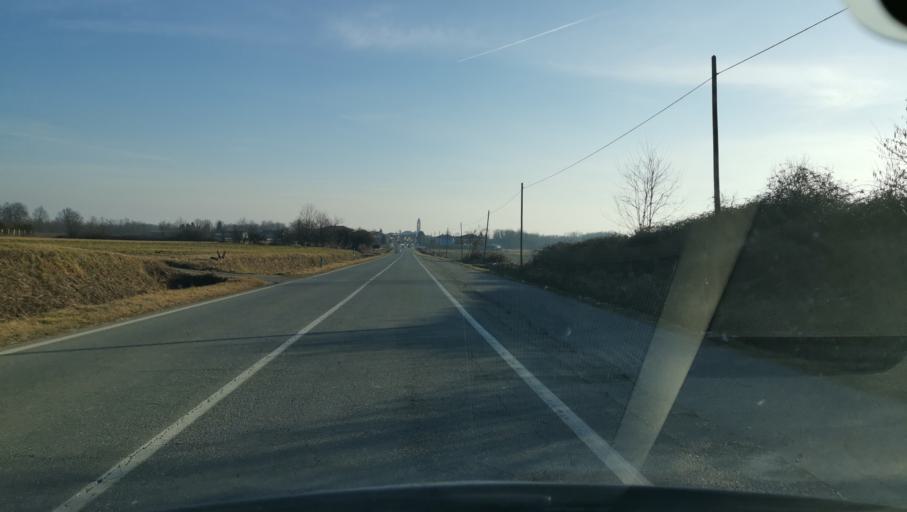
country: IT
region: Piedmont
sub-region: Provincia di Torino
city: Foglizzo
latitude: 45.2869
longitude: 7.8214
